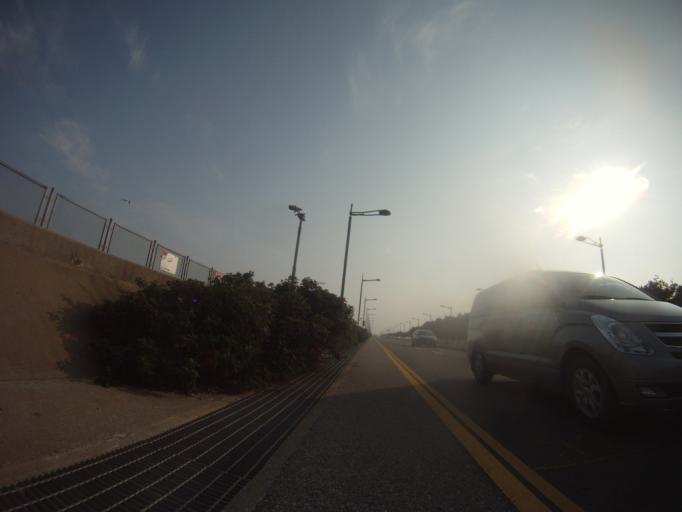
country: KR
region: Incheon
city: Incheon
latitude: 37.4293
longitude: 126.4567
